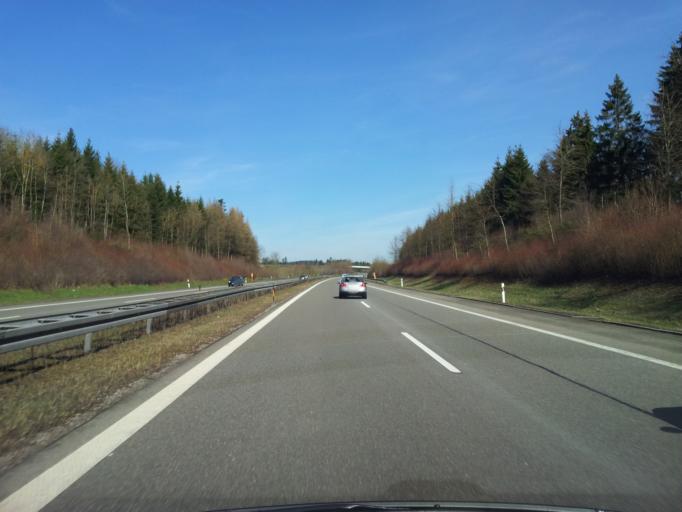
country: DE
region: Baden-Wuerttemberg
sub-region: Freiburg Region
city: Deisslingen
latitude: 48.1263
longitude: 8.5746
